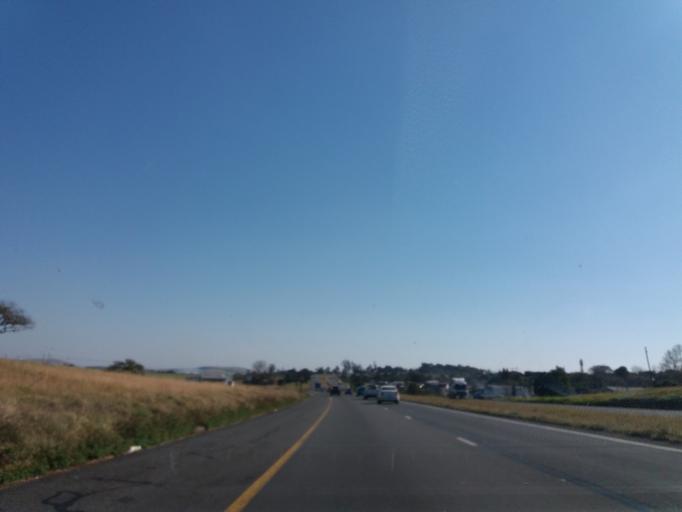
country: ZA
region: KwaZulu-Natal
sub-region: uMgungundlovu District Municipality
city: Camperdown
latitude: -29.7306
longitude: 30.5345
